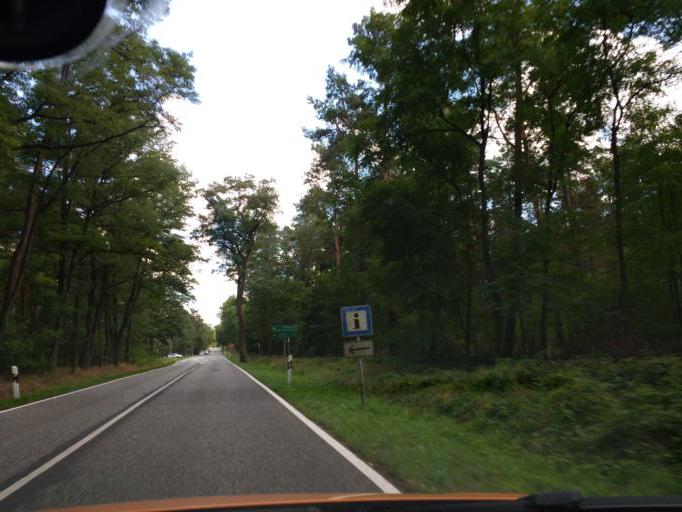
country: DE
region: Brandenburg
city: Wendisch Rietz
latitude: 52.2085
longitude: 14.0028
